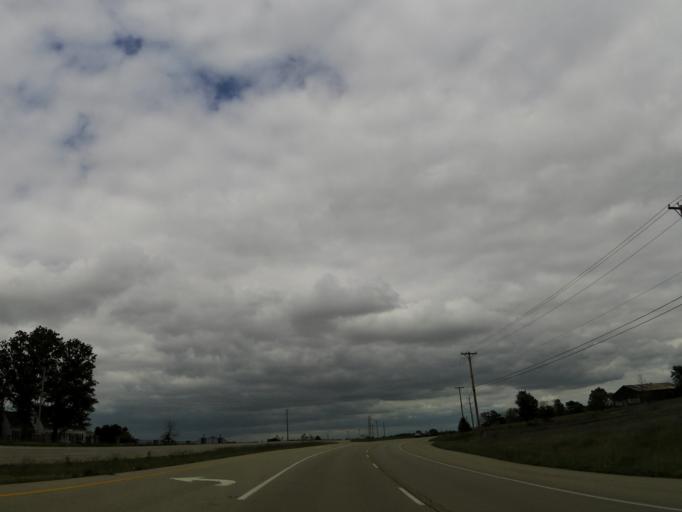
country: US
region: Kentucky
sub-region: Scott County
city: Georgetown
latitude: 38.1646
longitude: -84.6080
